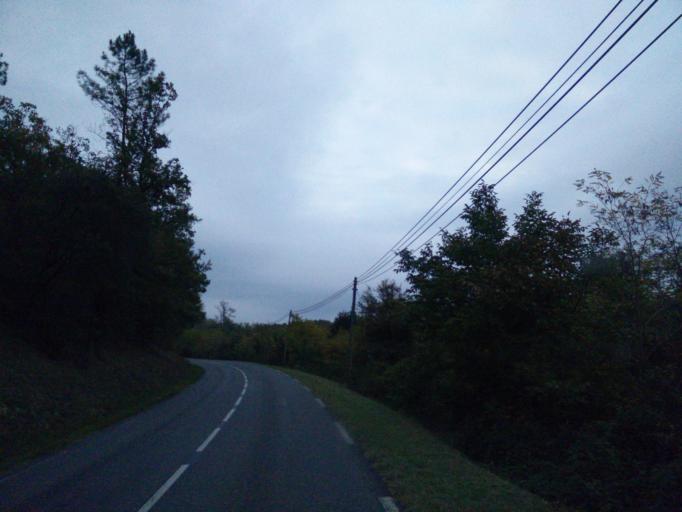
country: FR
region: Aquitaine
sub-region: Departement de la Dordogne
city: Carsac-Aillac
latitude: 44.7853
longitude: 1.3133
